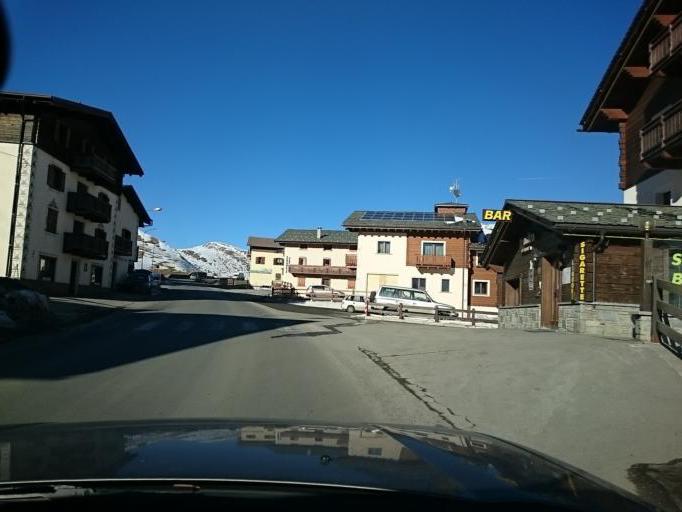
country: IT
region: Lombardy
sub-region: Provincia di Sondrio
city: Livigno
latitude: 46.5197
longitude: 10.1791
